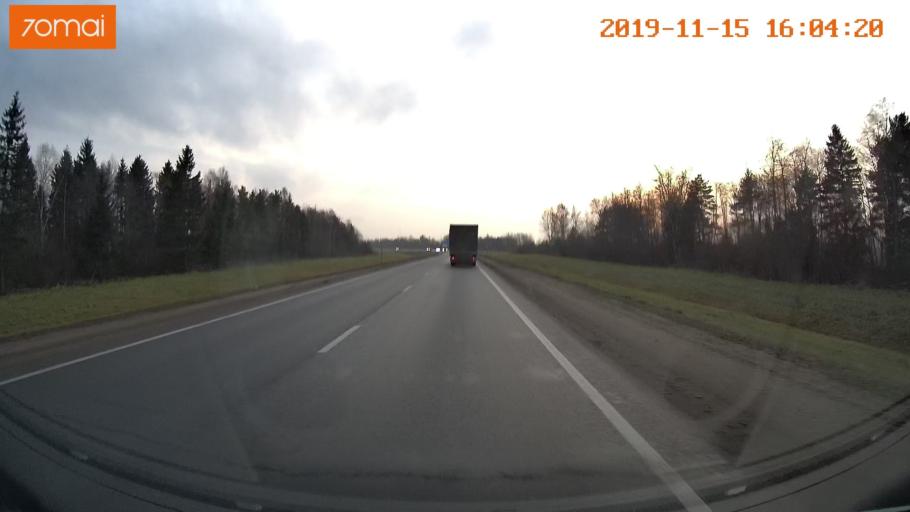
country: RU
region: Jaroslavl
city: Yaroslavl
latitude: 57.7490
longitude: 39.9029
